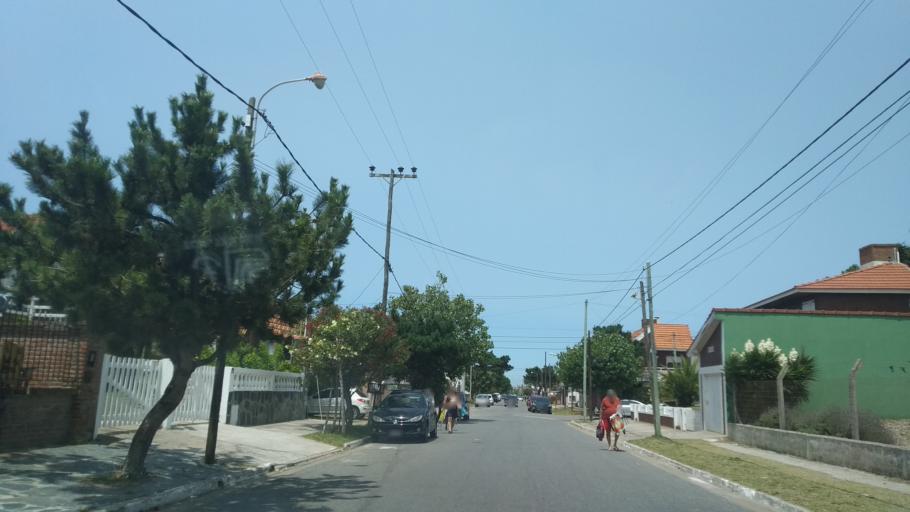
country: AR
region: Buenos Aires
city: Mar del Tuyu
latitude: -36.5596
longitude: -56.6894
